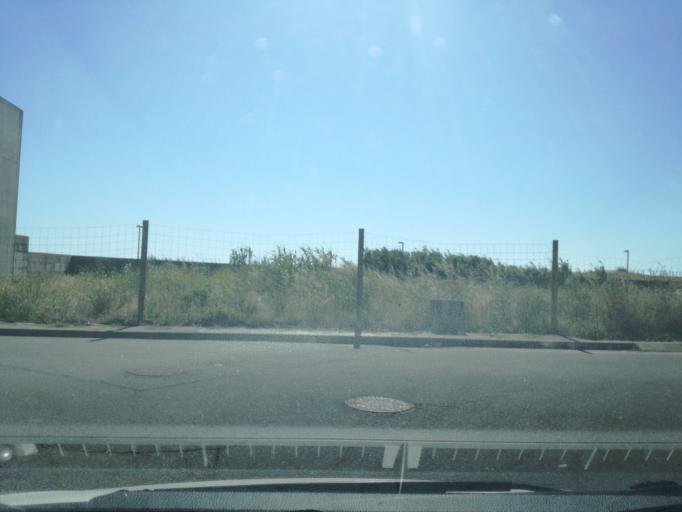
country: PT
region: Porto
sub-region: Matosinhos
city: Lavra
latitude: 41.2717
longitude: -8.7266
